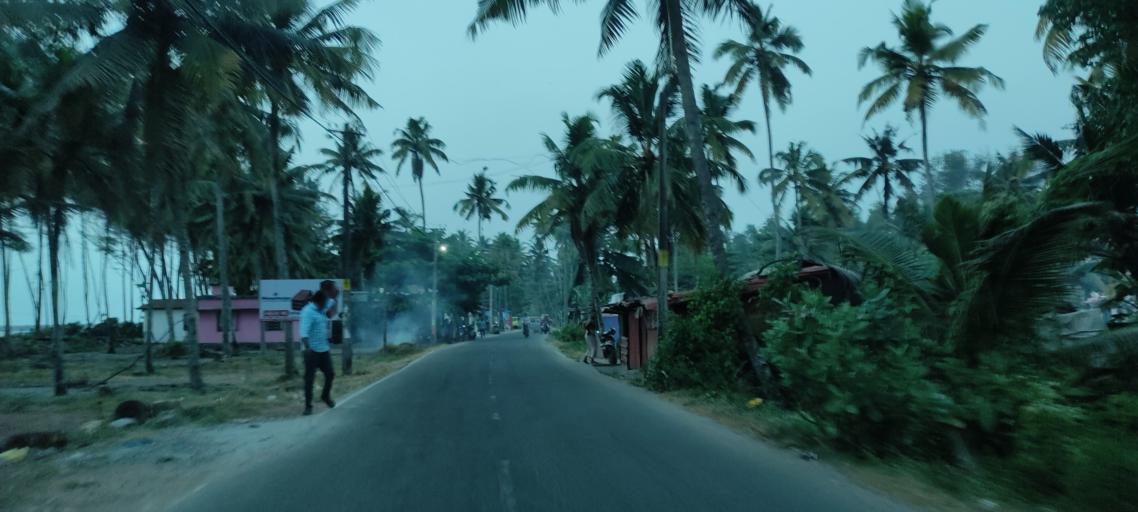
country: IN
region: Kerala
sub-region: Alappuzha
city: Kayankulam
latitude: 9.1306
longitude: 76.4656
